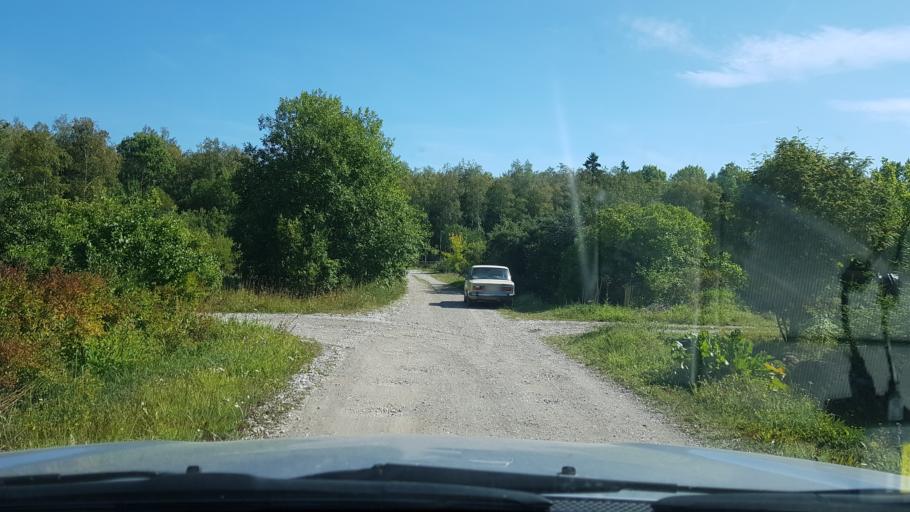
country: EE
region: Ida-Virumaa
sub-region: Sillamaee linn
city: Sillamae
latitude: 59.3714
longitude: 27.7961
